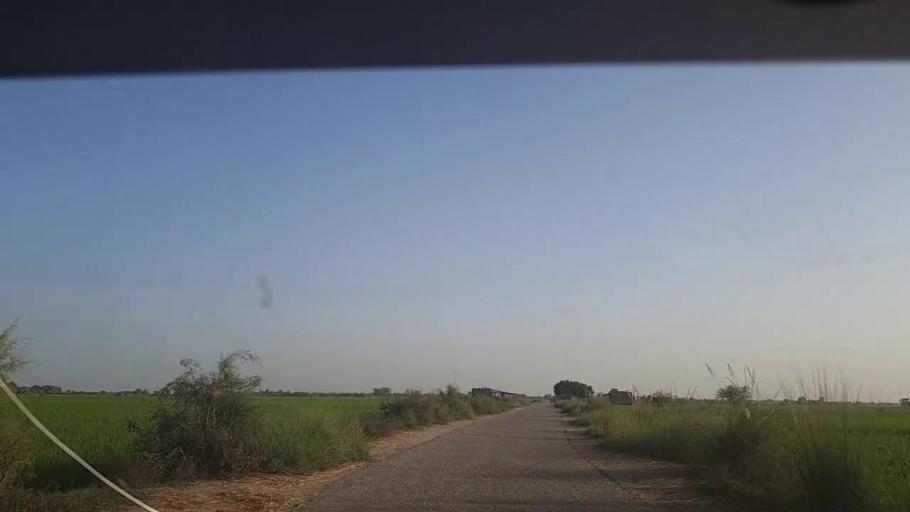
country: PK
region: Sindh
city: Thul
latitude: 28.1977
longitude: 68.8740
